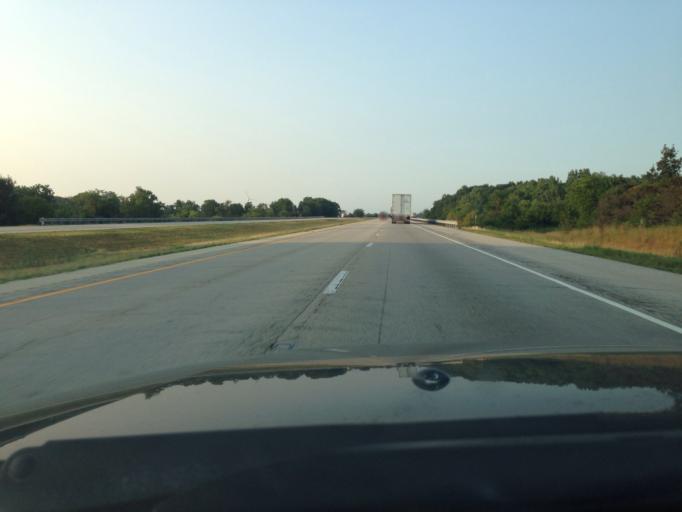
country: US
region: Illinois
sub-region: Ford County
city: Paxton
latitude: 40.5129
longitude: -88.0847
